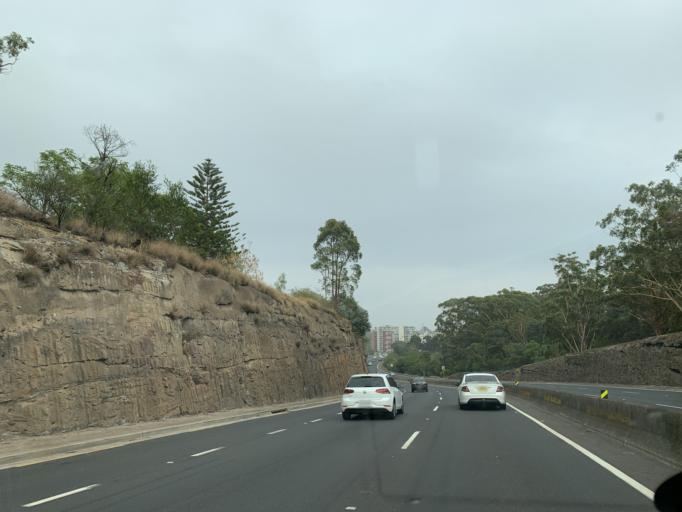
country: AU
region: New South Wales
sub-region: Parramatta
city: Northmead
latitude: -33.7925
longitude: 151.0062
